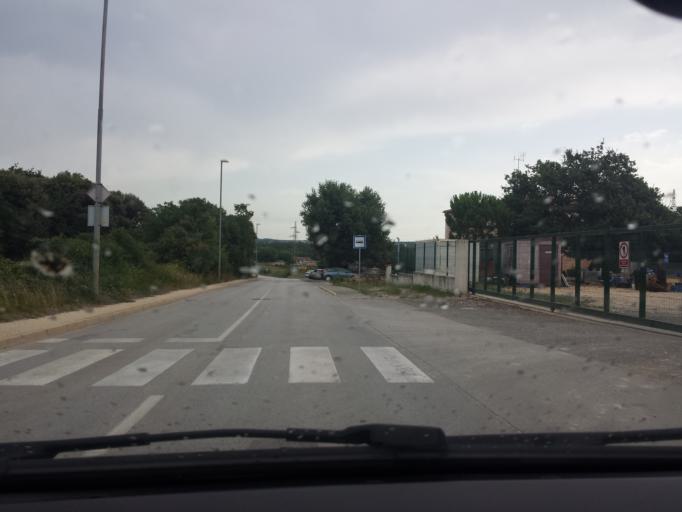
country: HR
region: Istarska
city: Galizana
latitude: 44.9055
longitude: 13.8547
